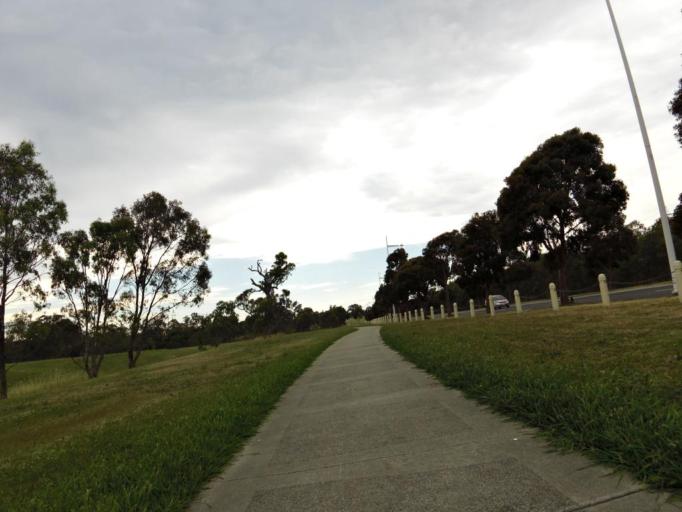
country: AU
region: Victoria
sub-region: Whittlesea
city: Mill Park
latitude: -37.6415
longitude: 145.0722
